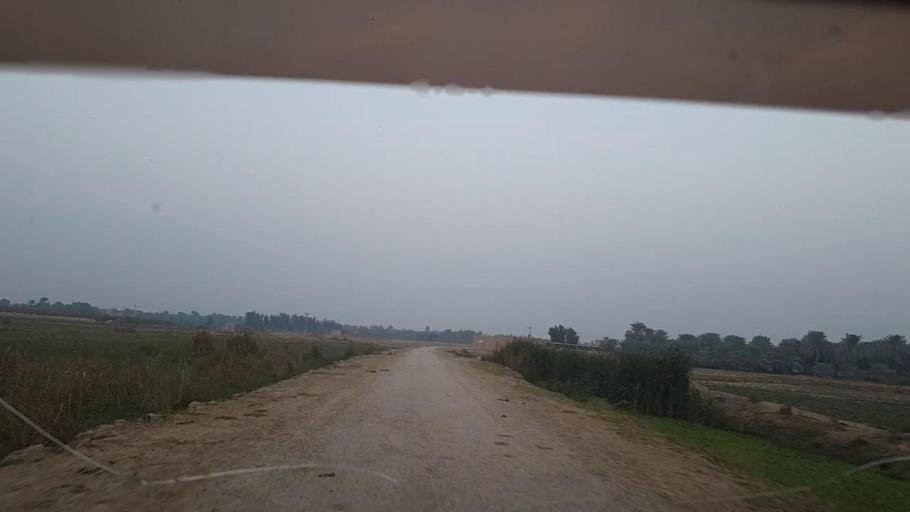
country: PK
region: Sindh
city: Khairpur
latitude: 27.5759
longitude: 68.7296
